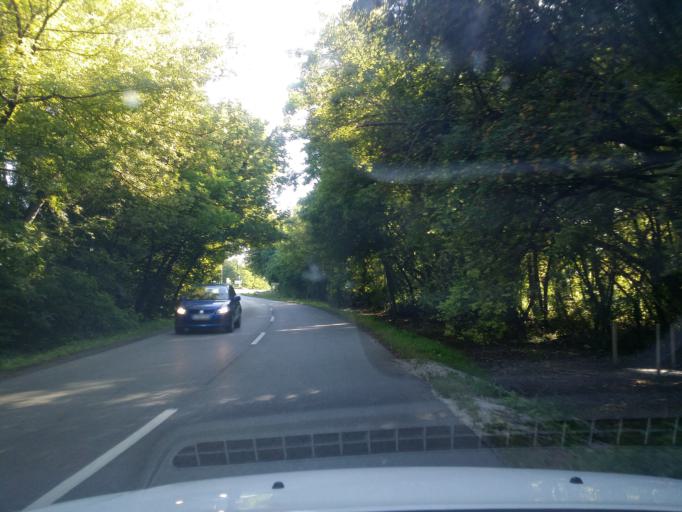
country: HU
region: Fejer
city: Sarbogard
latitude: 46.8477
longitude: 18.5643
